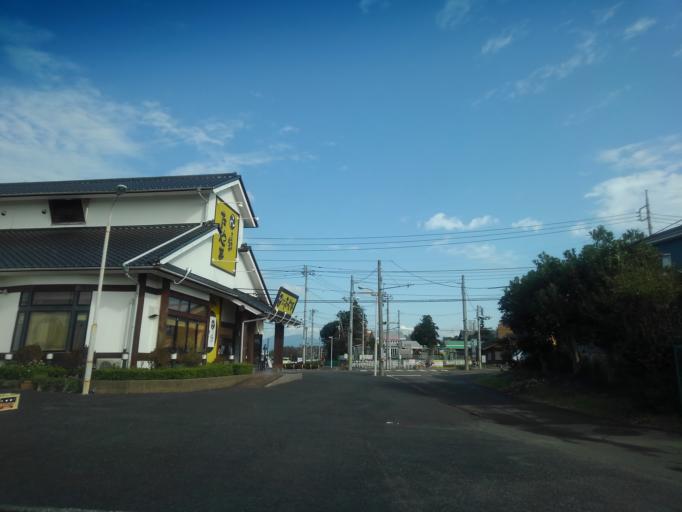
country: JP
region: Ibaraki
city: Naka
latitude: 36.0713
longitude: 140.0868
